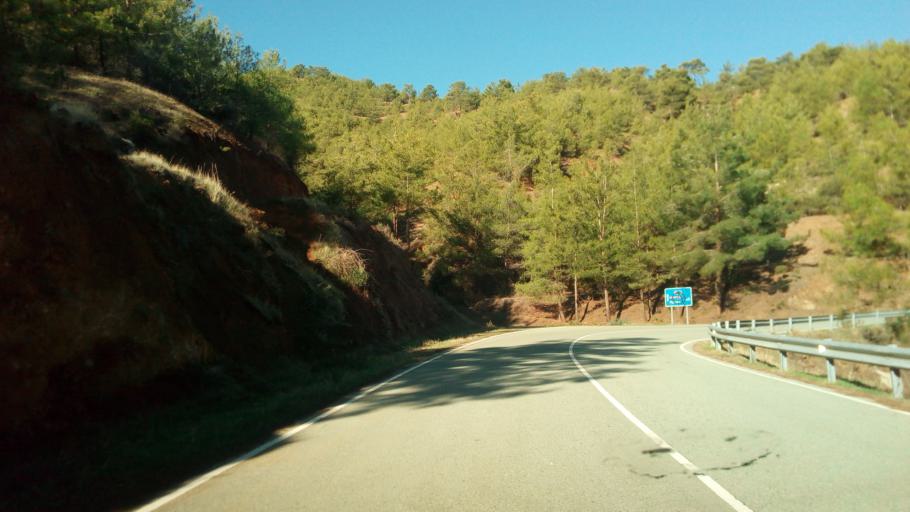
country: CY
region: Lefkosia
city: Lefka
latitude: 35.0850
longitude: 32.7811
